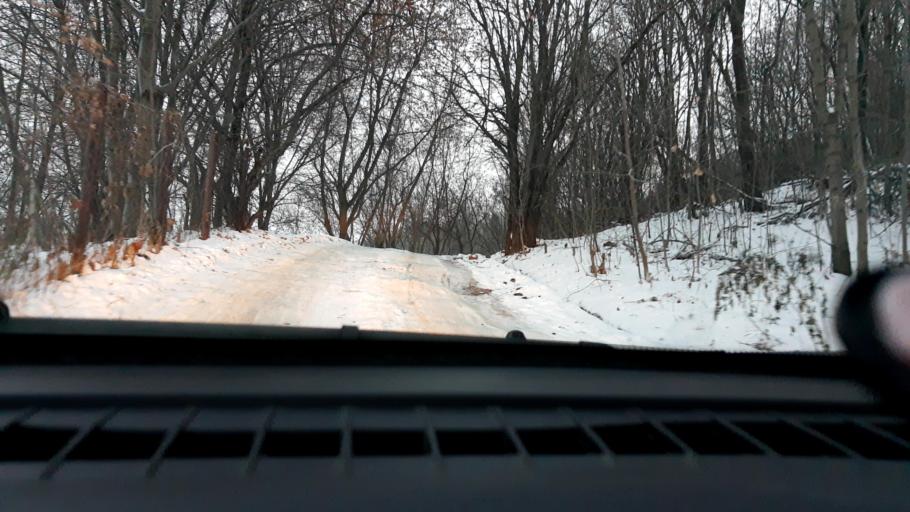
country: RU
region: Nizjnij Novgorod
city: Bor
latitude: 56.3188
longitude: 44.0702
